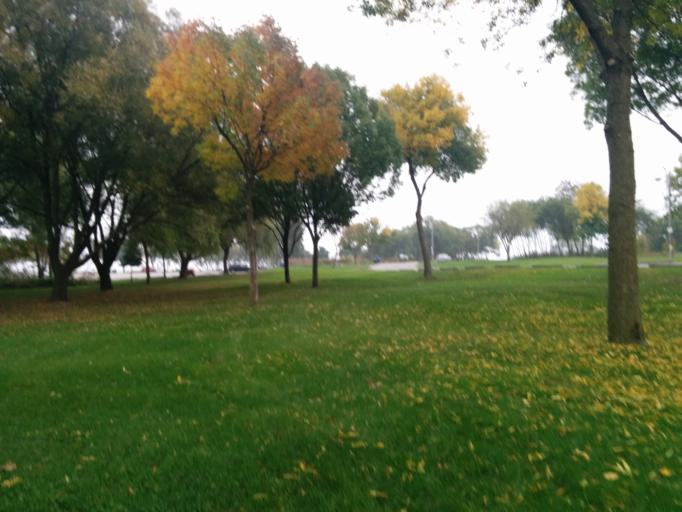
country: CA
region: Ontario
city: Etobicoke
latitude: 43.5860
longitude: -79.5440
